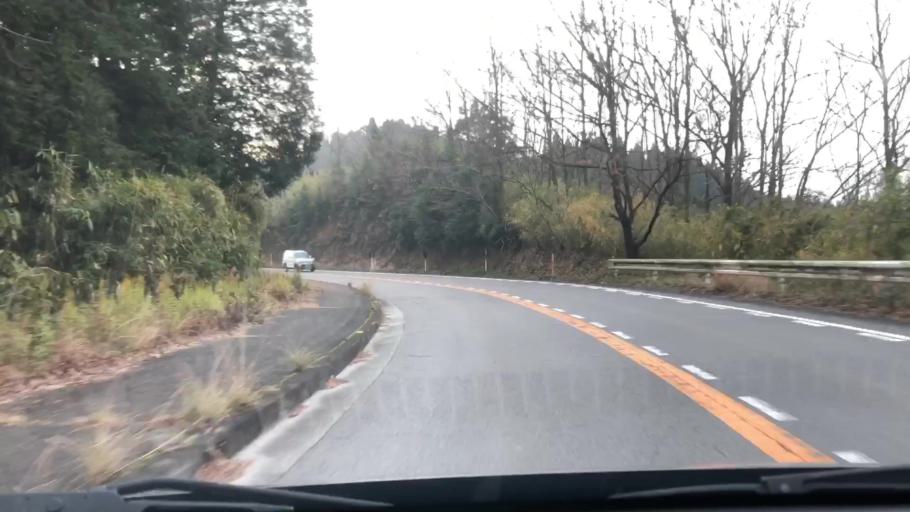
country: JP
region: Oita
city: Takedamachi
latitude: 32.9700
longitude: 131.5054
